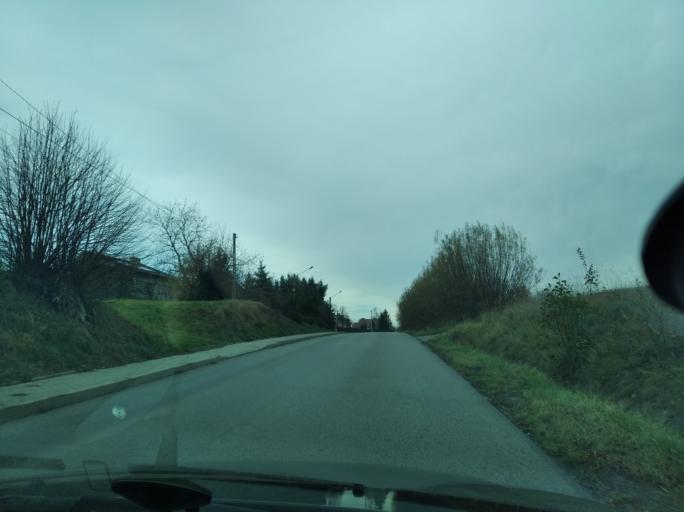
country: PL
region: Subcarpathian Voivodeship
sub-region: Powiat lancucki
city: Albigowa
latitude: 50.0328
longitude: 22.2349
